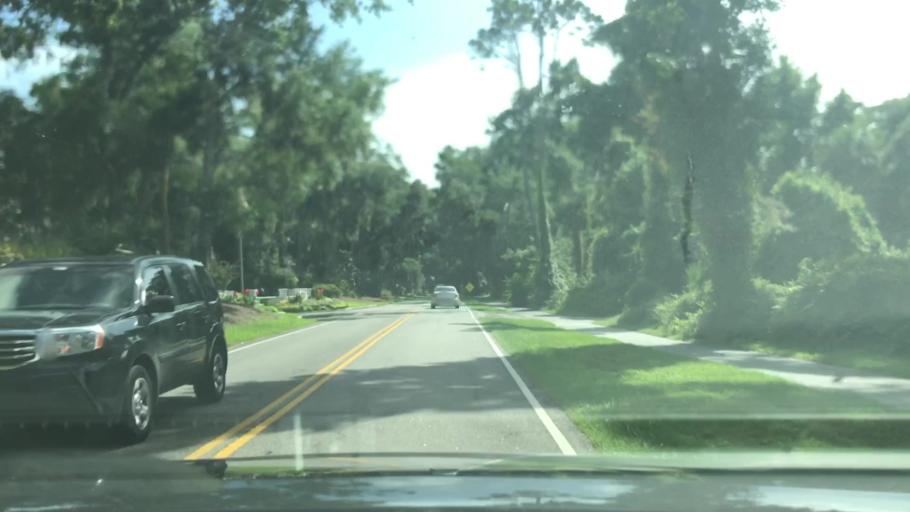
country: US
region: South Carolina
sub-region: Beaufort County
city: Hilton Head Island
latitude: 32.1428
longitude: -80.7637
